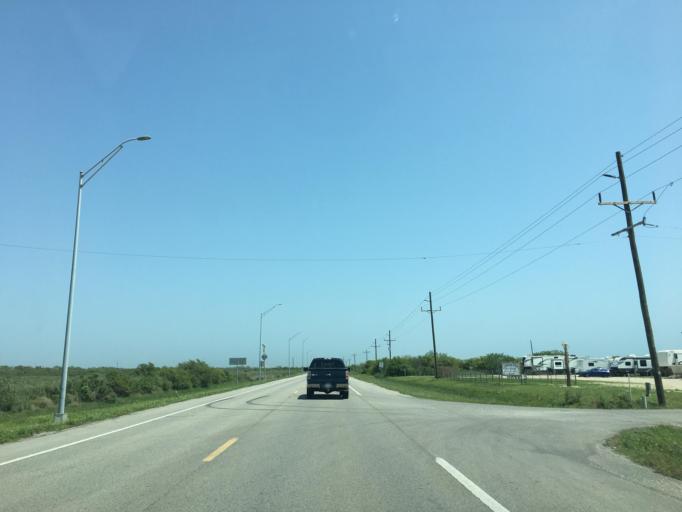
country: US
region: Texas
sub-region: Galveston County
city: Galveston
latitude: 29.3771
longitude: -94.7492
